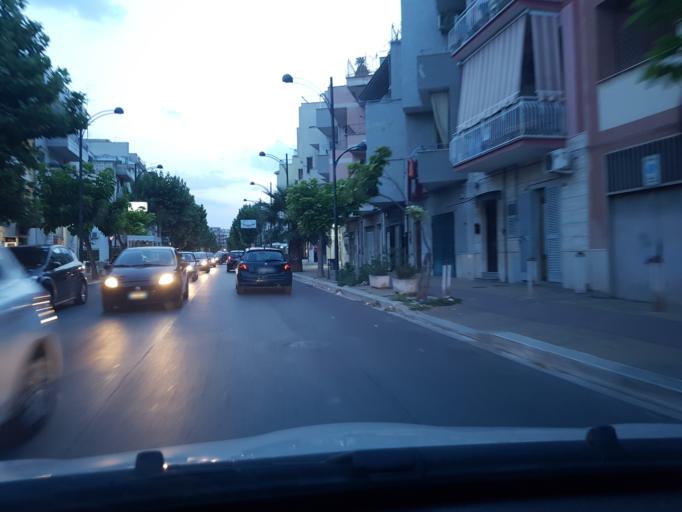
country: IT
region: Apulia
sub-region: Provincia di Foggia
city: Cerignola
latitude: 41.2606
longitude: 15.9029
